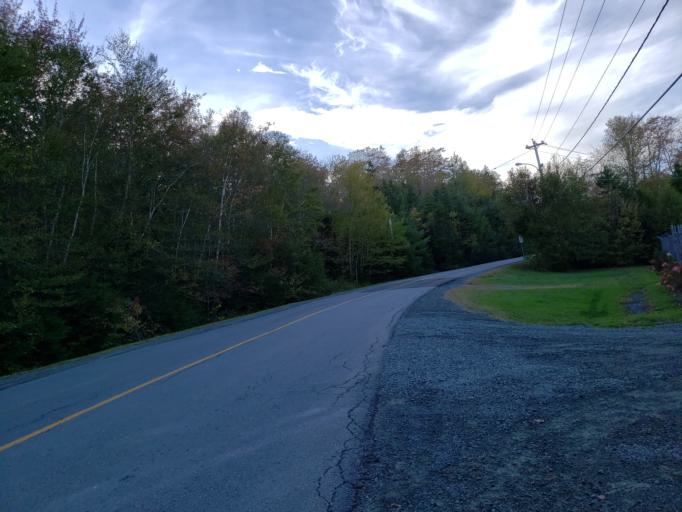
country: CA
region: Nova Scotia
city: Cole Harbour
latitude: 44.7436
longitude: -63.3796
